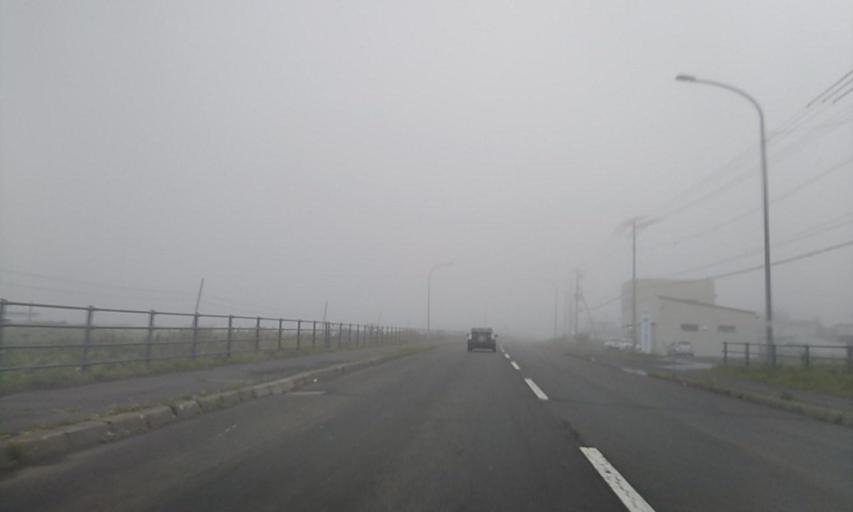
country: JP
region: Hokkaido
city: Nemuro
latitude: 43.3036
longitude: 145.5918
